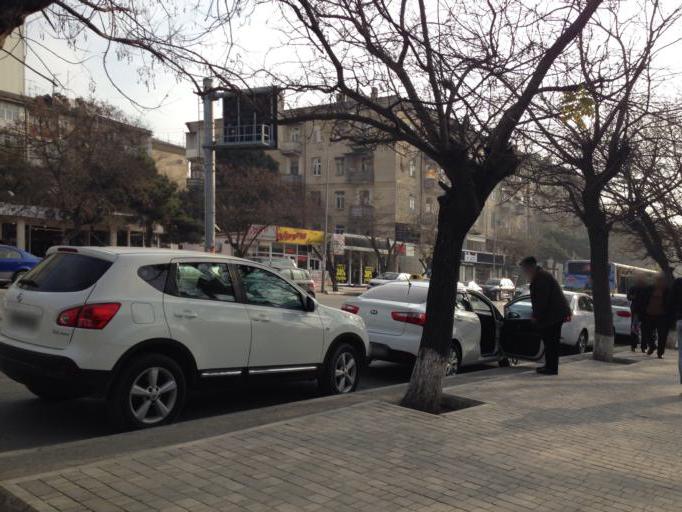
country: AZ
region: Baki
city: Baku
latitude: 40.4027
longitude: 49.8722
